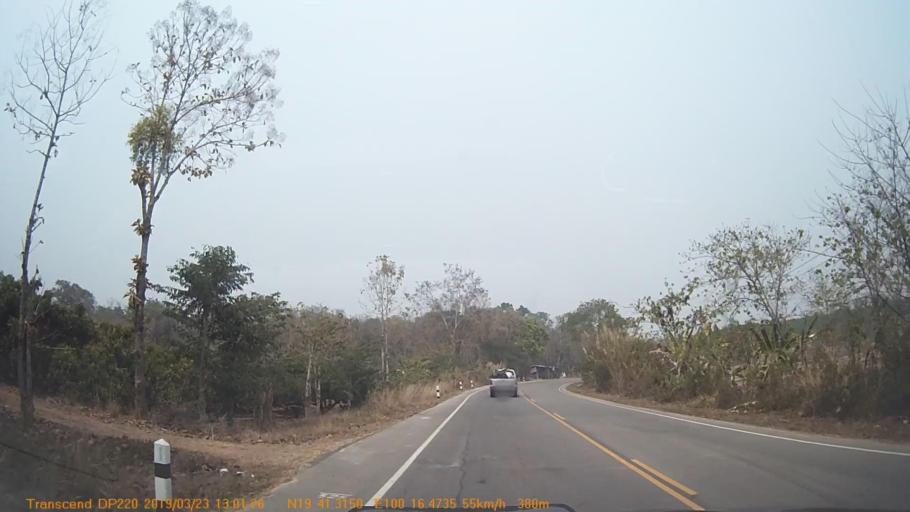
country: TH
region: Chiang Rai
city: Thoeng
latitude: 19.6889
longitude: 100.2746
